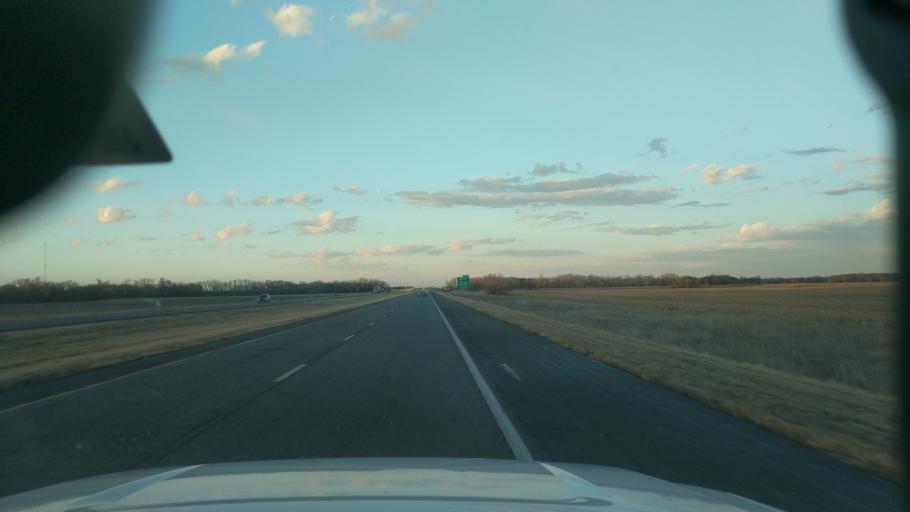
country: US
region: Kansas
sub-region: McPherson County
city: Lindsborg
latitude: 38.6035
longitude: -97.6211
